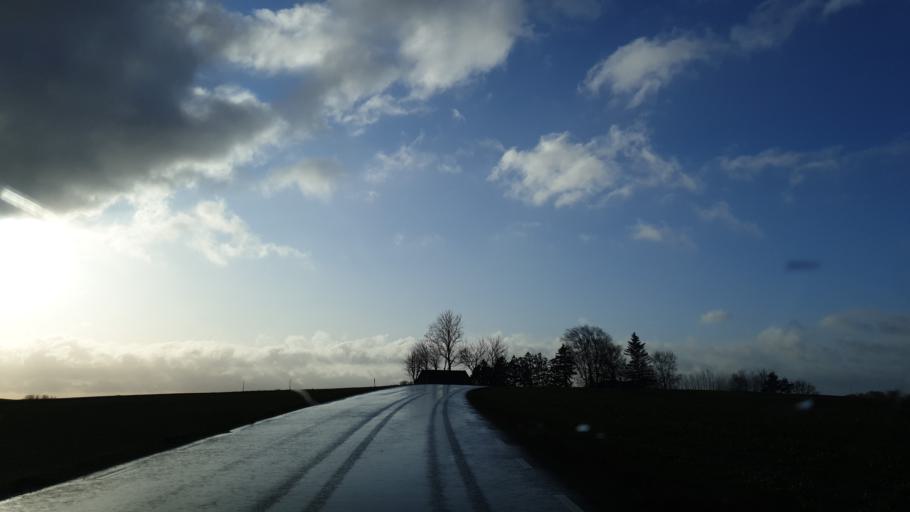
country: SE
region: Skane
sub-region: Skurups Kommun
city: Rydsgard
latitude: 55.4609
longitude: 13.5591
